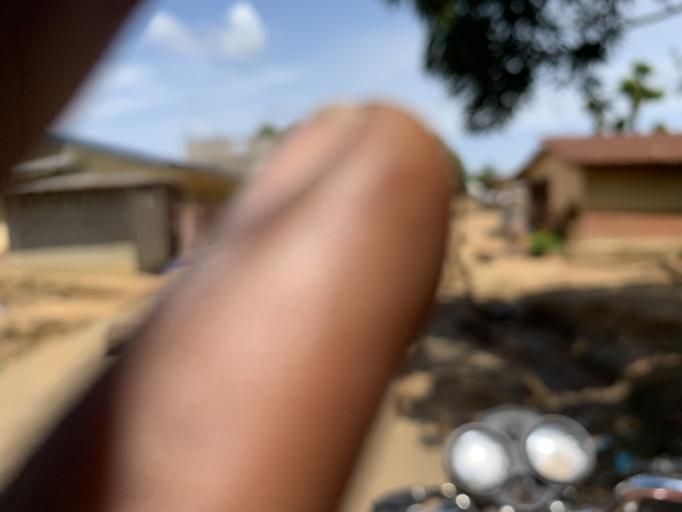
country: SL
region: Western Area
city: Waterloo
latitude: 8.3382
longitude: -13.0460
